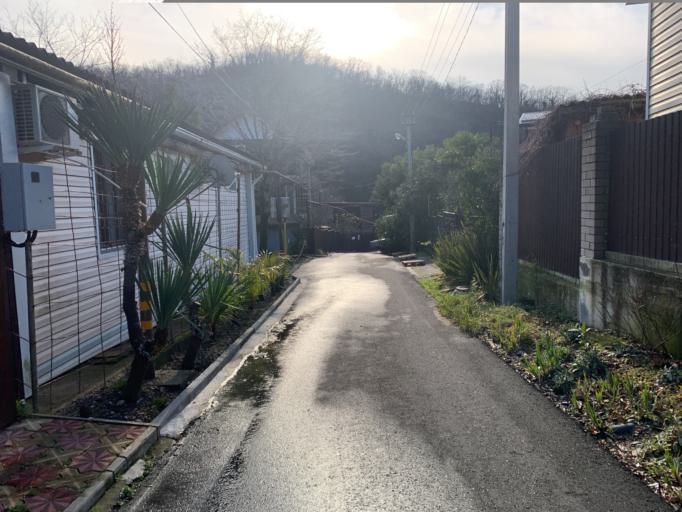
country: RU
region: Krasnodarskiy
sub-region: Sochi City
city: Lazarevskoye
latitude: 43.9235
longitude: 39.3234
